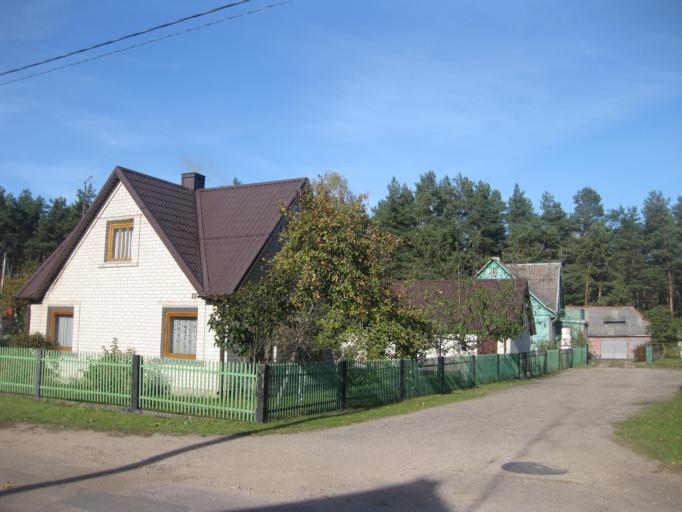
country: LT
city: Ezerelis
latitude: 54.8845
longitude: 23.5962
